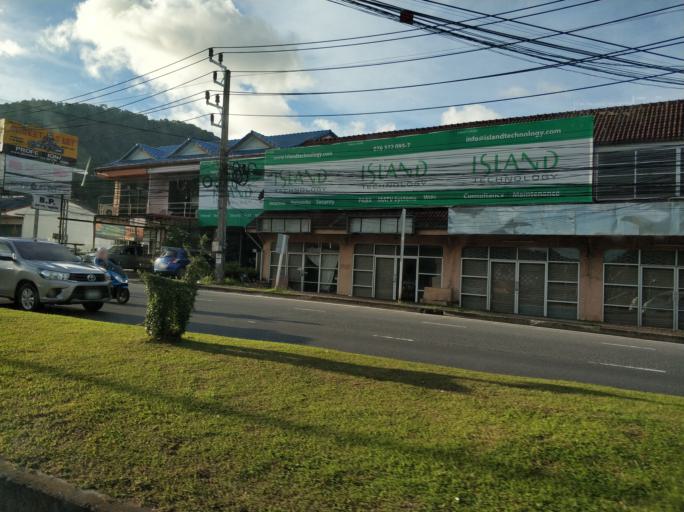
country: TH
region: Phuket
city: Kathu
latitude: 7.9076
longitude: 98.3297
